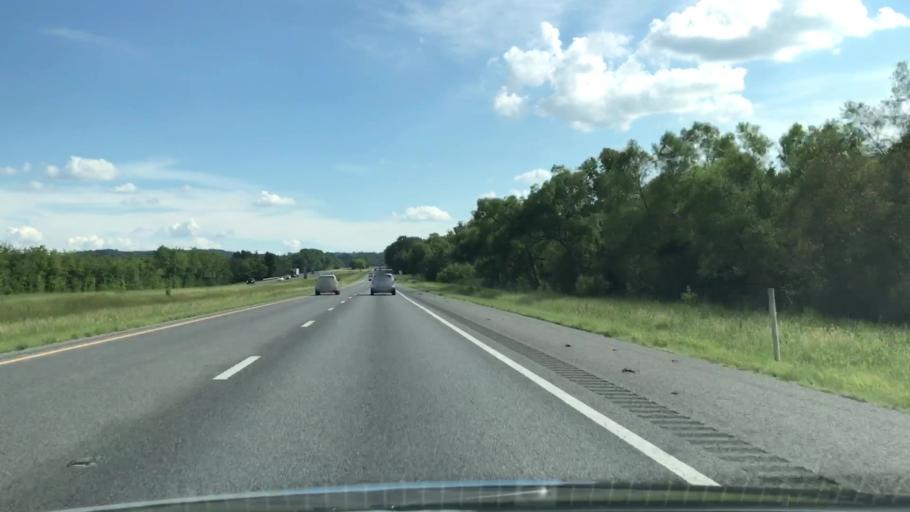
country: US
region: Tennessee
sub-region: Marshall County
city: Cornersville
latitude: 35.4312
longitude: -86.8803
